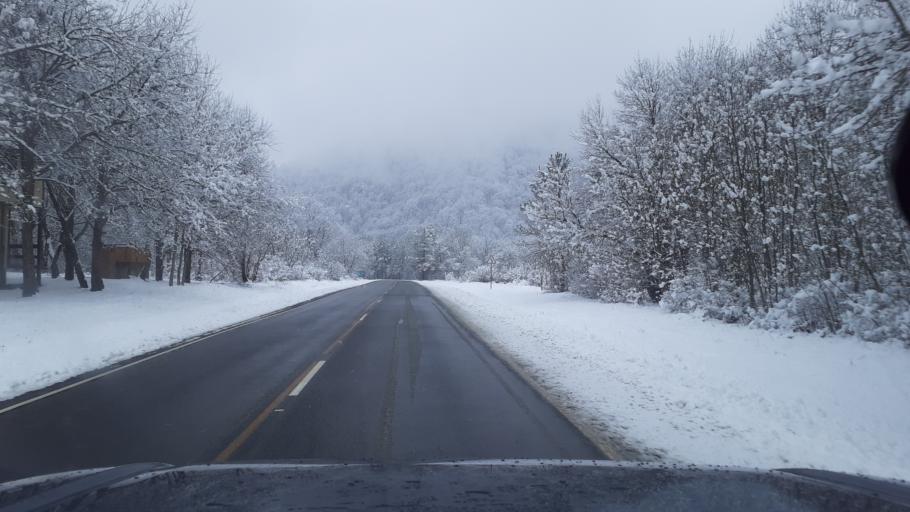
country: RU
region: Adygeya
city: Kamennomostskiy
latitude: 44.1744
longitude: 40.1518
